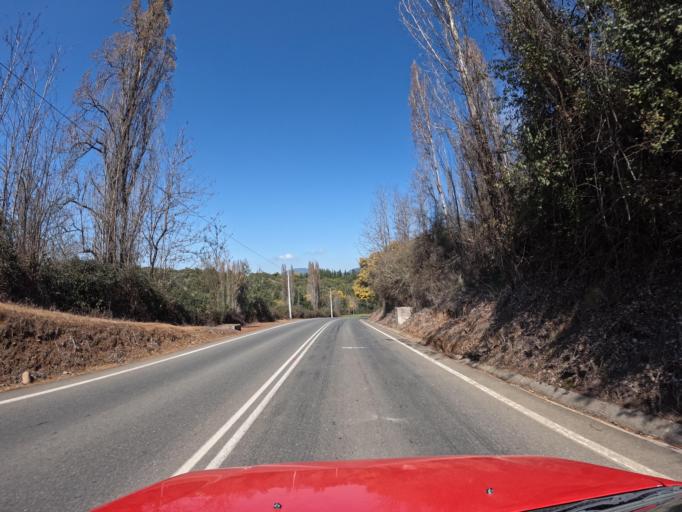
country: CL
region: Maule
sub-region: Provincia de Talca
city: San Clemente
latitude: -35.4551
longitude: -71.2691
